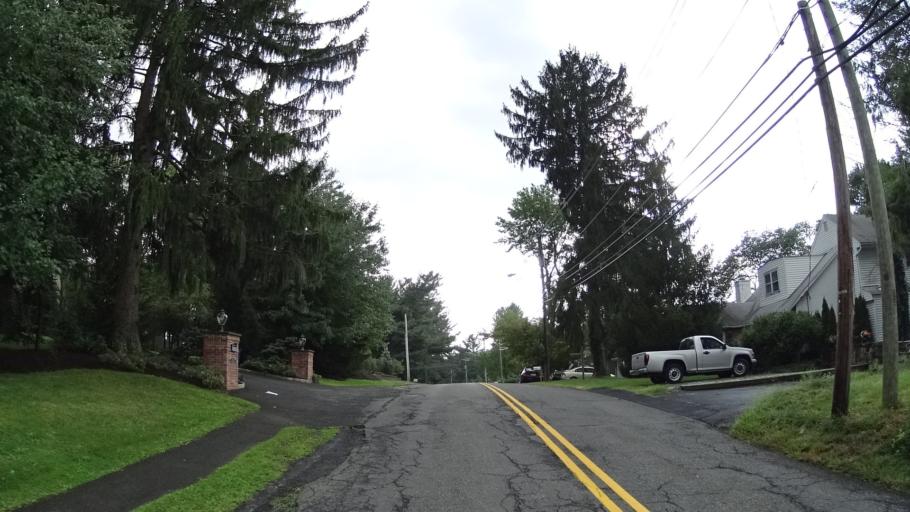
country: US
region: New Jersey
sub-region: Union County
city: Berkeley Heights
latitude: 40.7028
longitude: -74.4384
